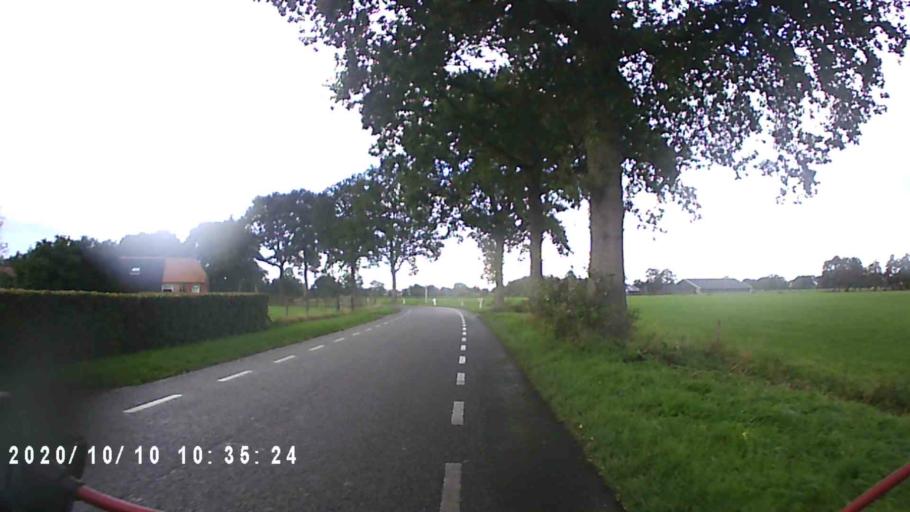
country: NL
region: Groningen
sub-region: Gemeente Grootegast
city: Grootegast
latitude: 53.1892
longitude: 6.3094
